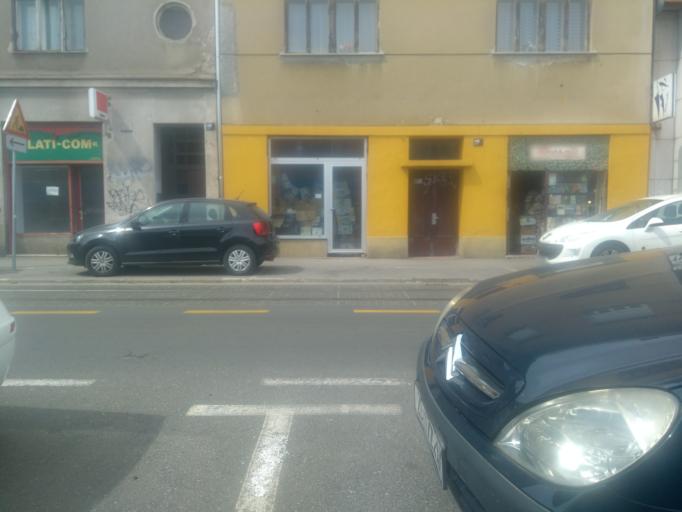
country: HR
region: Grad Zagreb
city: Zagreb - Centar
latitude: 45.8018
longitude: 15.9591
